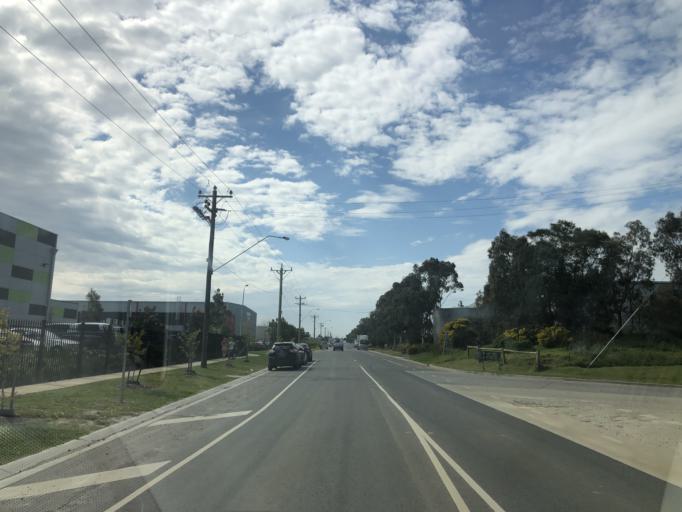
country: AU
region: Victoria
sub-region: Casey
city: Hampton Park
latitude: -38.0402
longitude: 145.2277
